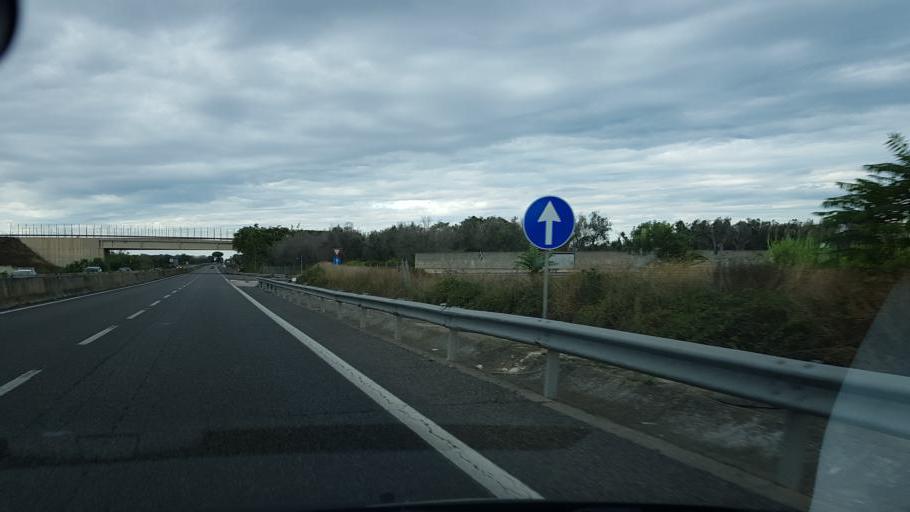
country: IT
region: Apulia
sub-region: Provincia di Brindisi
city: Torchiarolo
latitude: 40.4846
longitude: 18.0421
